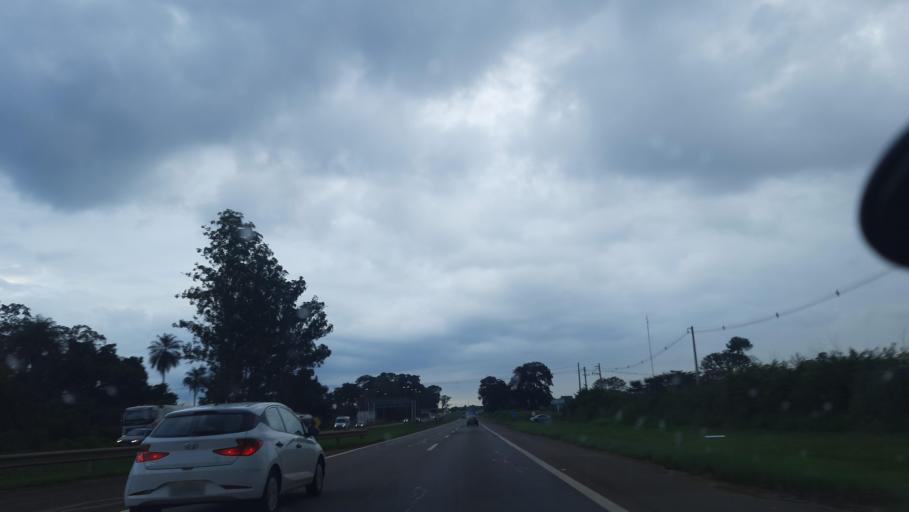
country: BR
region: Sao Paulo
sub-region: Santo Antonio De Posse
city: Santo Antonio de Posse
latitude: -22.5631
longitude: -47.0005
